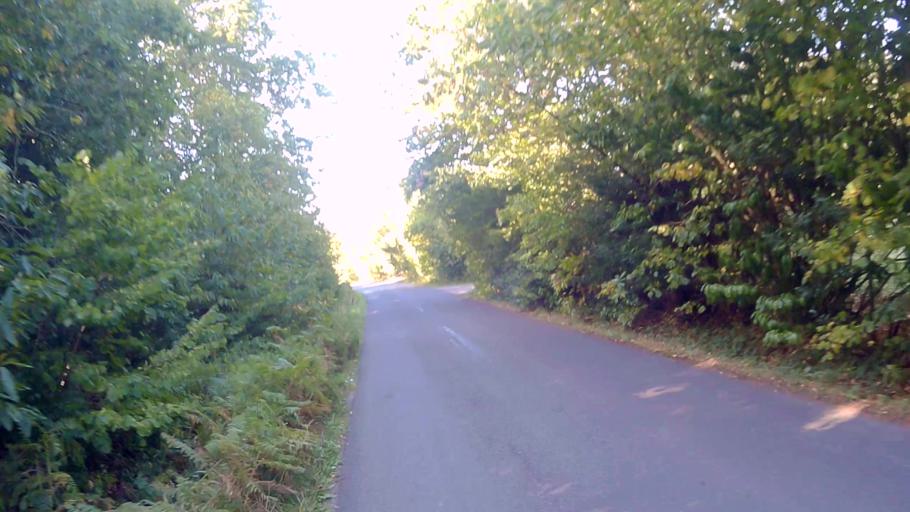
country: GB
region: England
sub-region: Hampshire
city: Kingsley
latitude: 51.1640
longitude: -0.8419
